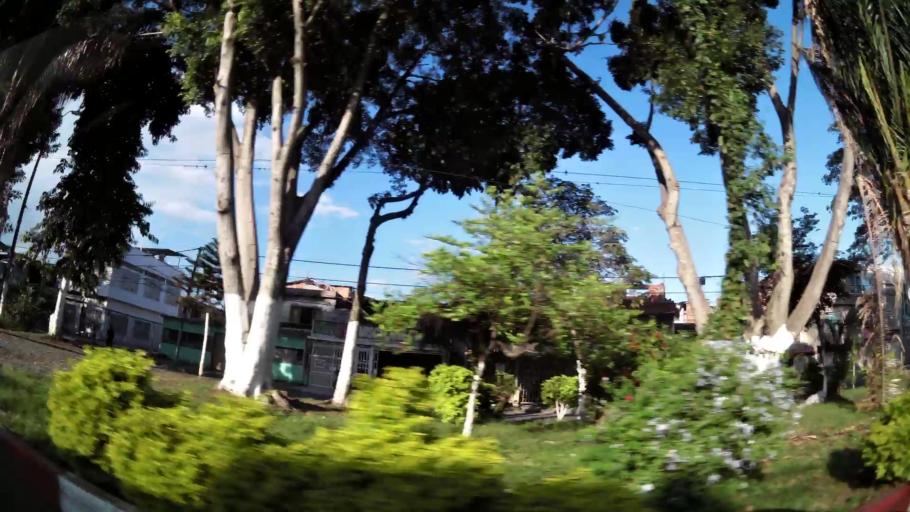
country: CO
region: Valle del Cauca
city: Cali
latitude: 3.4143
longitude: -76.5099
